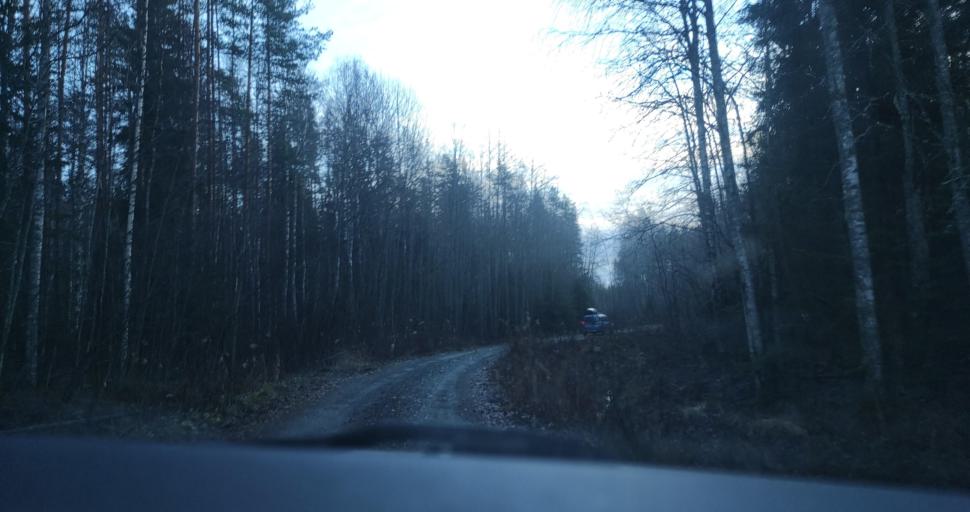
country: RU
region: Republic of Karelia
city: Pitkyaranta
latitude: 61.7332
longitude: 31.3735
